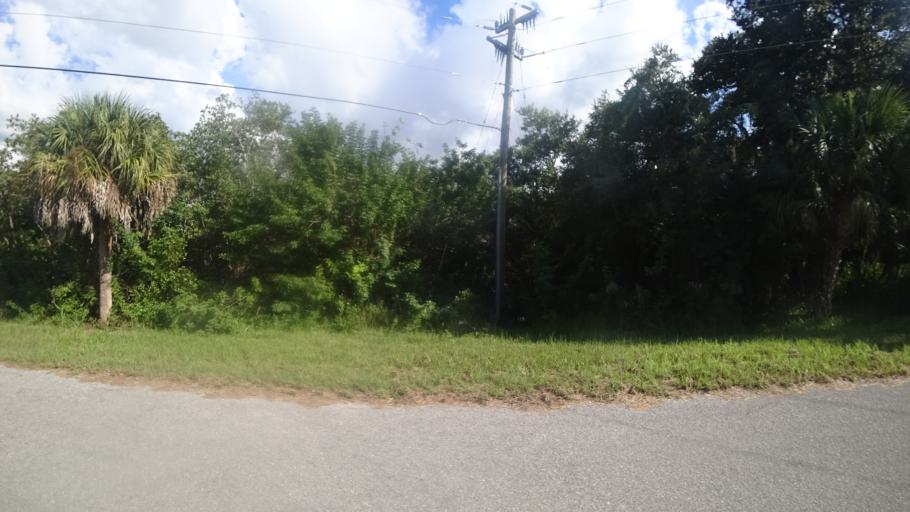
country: US
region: Florida
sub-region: Manatee County
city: Memphis
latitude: 27.5718
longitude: -82.5849
